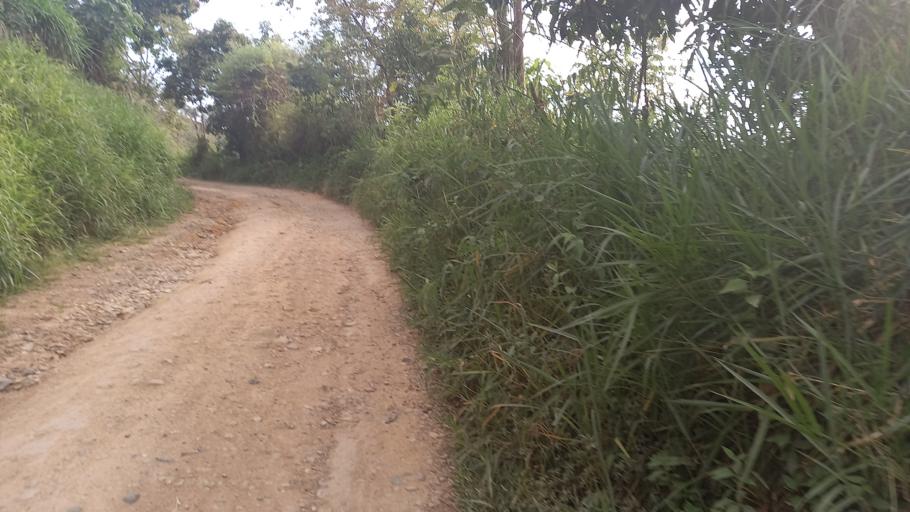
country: CO
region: Antioquia
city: Santa Barbara
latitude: 5.8324
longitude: -75.5780
